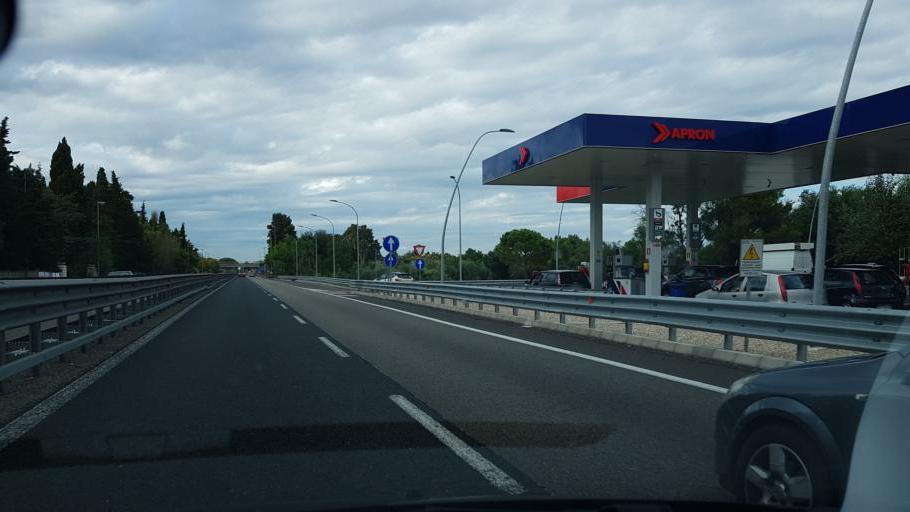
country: IT
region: Apulia
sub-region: Provincia di Lecce
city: Cavallino
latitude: 40.3043
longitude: 18.1920
